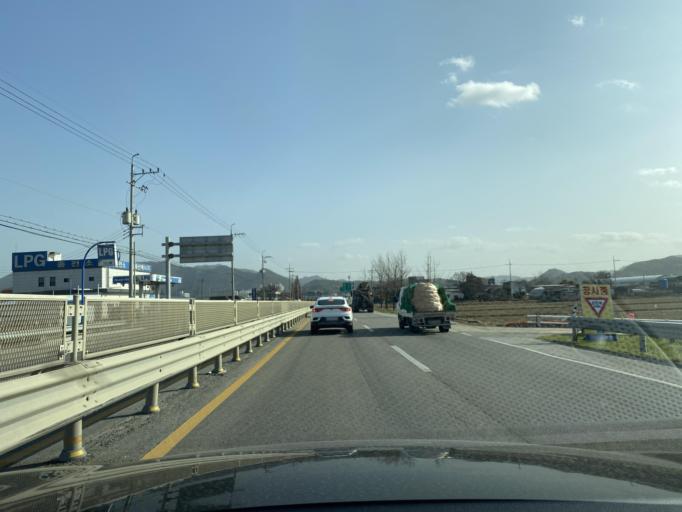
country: KR
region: Chungcheongnam-do
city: Yesan
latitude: 36.6849
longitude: 126.8127
